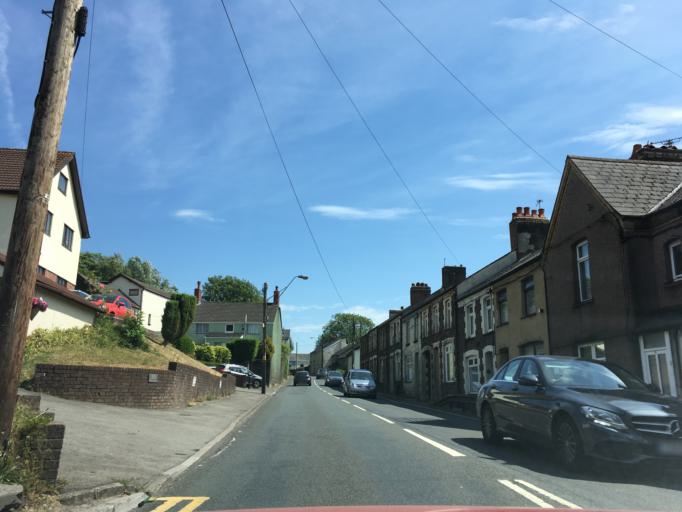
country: GB
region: Wales
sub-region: Newport
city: Newport
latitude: 51.5911
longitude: -3.0493
